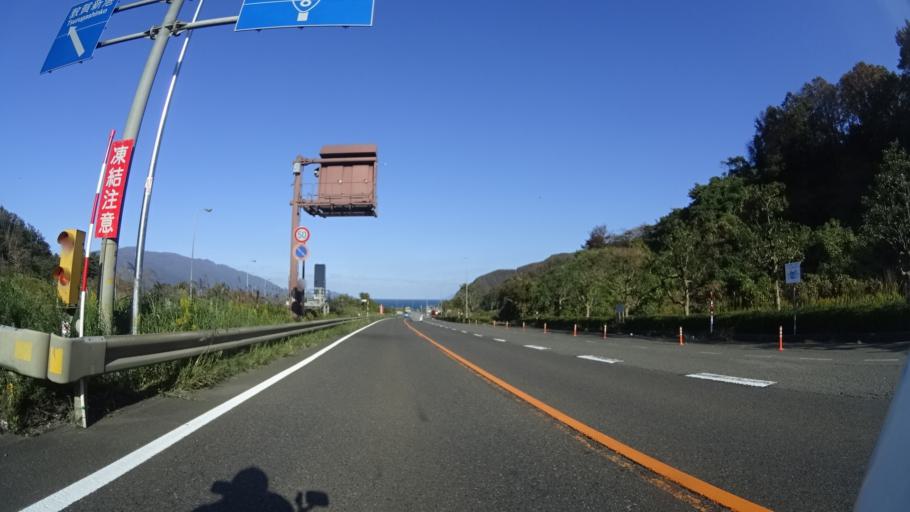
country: JP
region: Fukui
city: Tsuruga
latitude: 35.6746
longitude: 136.0878
